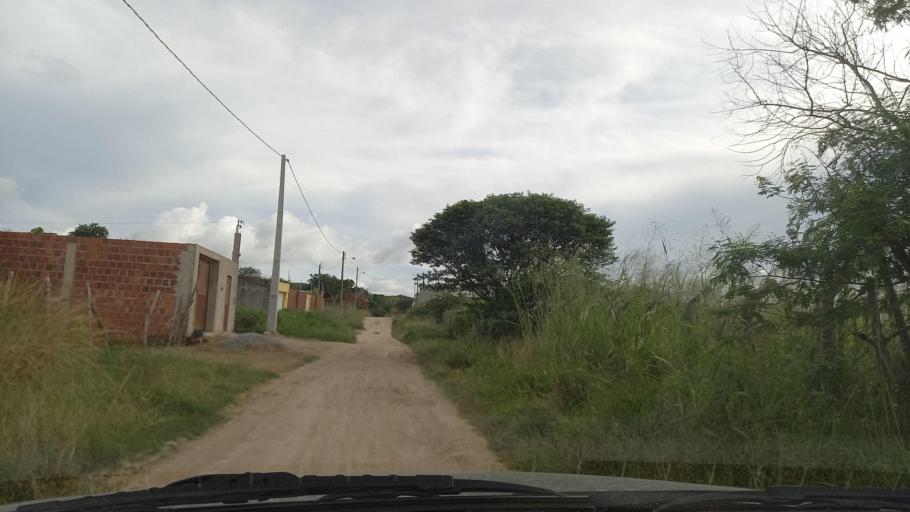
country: BR
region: Pernambuco
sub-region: Gravata
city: Gravata
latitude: -8.1989
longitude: -35.5364
